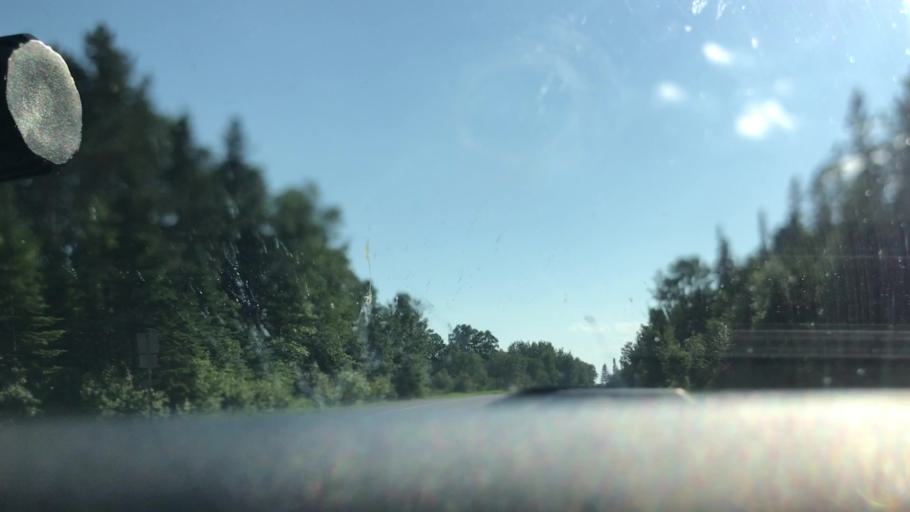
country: US
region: Minnesota
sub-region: Cook County
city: Grand Marais
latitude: 47.7991
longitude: -90.1049
